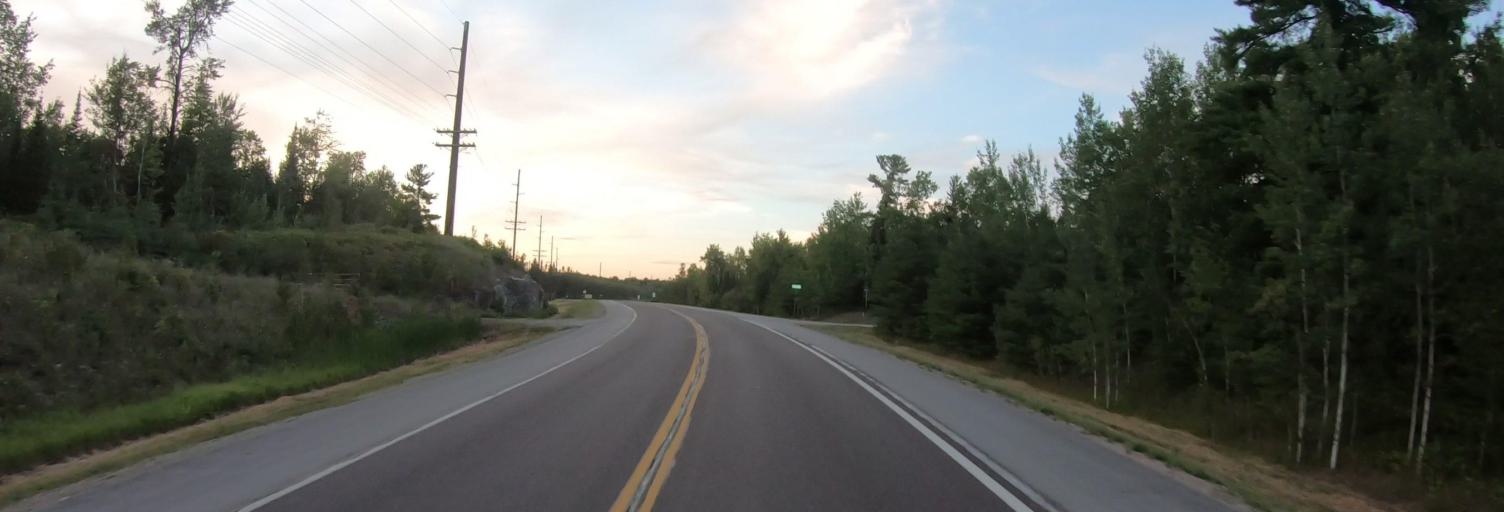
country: US
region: Minnesota
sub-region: Saint Louis County
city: Aurora
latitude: 47.8026
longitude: -92.3715
